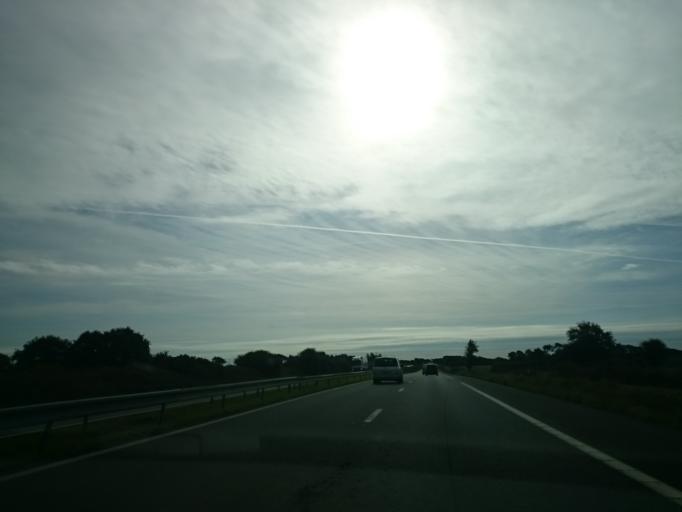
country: FR
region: Brittany
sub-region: Departement du Morbihan
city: Ambon
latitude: 47.5839
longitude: -2.5388
